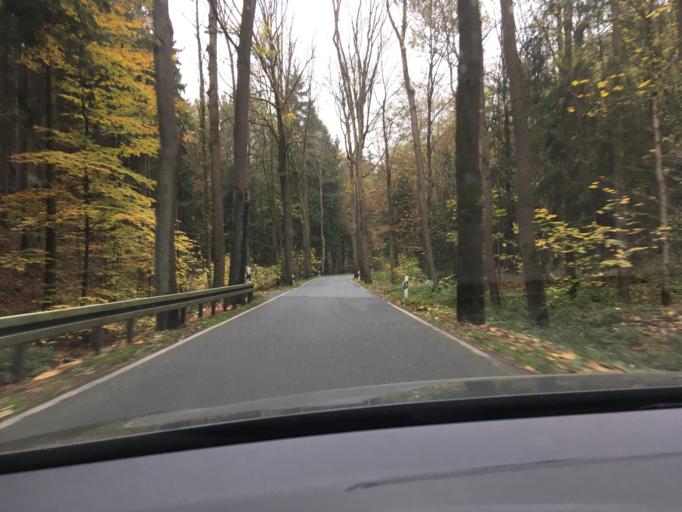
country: DE
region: Saxony
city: Reinhardtsgrimma
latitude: 50.8910
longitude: 13.7973
